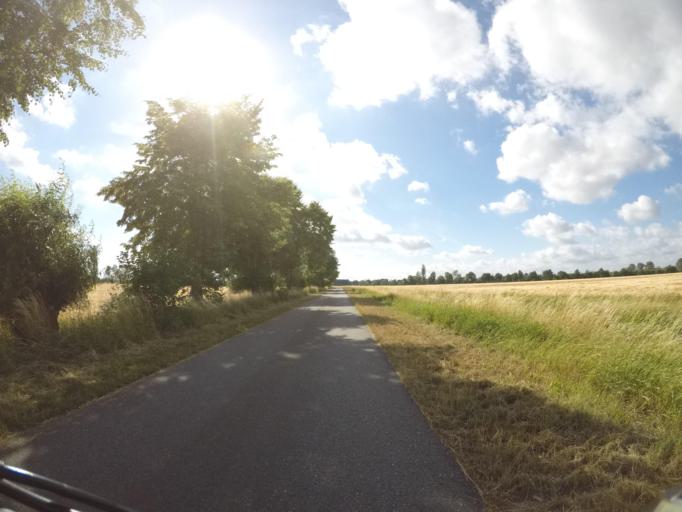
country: DE
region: Lower Saxony
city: Damnatz
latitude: 53.1829
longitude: 11.1596
